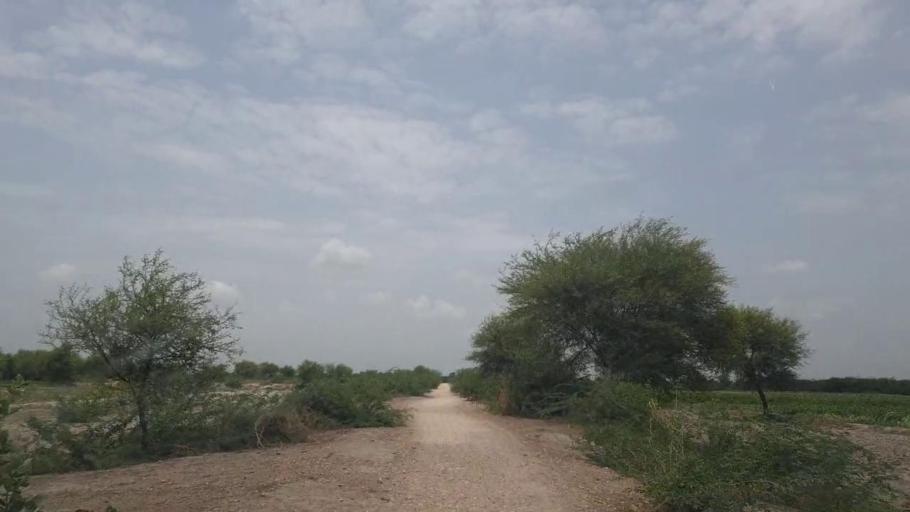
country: PK
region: Sindh
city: Naukot
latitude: 24.9367
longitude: 69.2007
